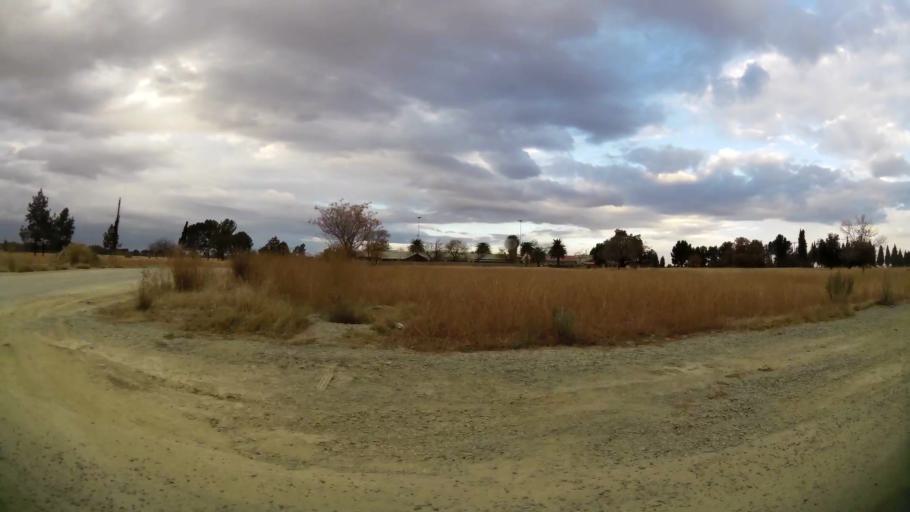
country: ZA
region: Orange Free State
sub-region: Lejweleputswa District Municipality
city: Welkom
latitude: -27.9689
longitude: 26.7010
